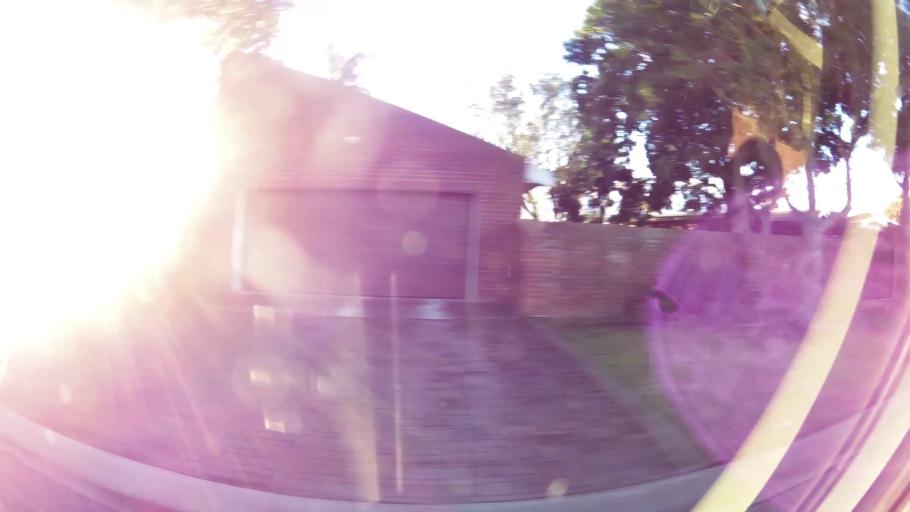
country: ZA
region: Eastern Cape
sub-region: Nelson Mandela Bay Metropolitan Municipality
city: Port Elizabeth
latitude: -33.9741
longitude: 25.4941
